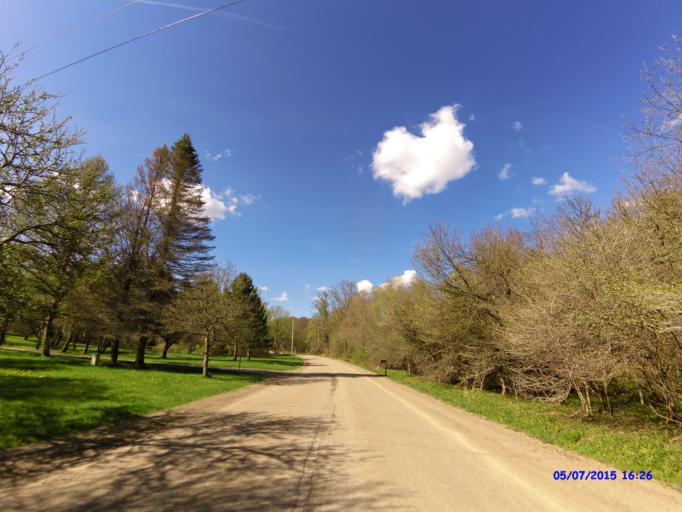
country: US
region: New York
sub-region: Cattaraugus County
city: Little Valley
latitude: 42.2958
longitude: -78.6781
